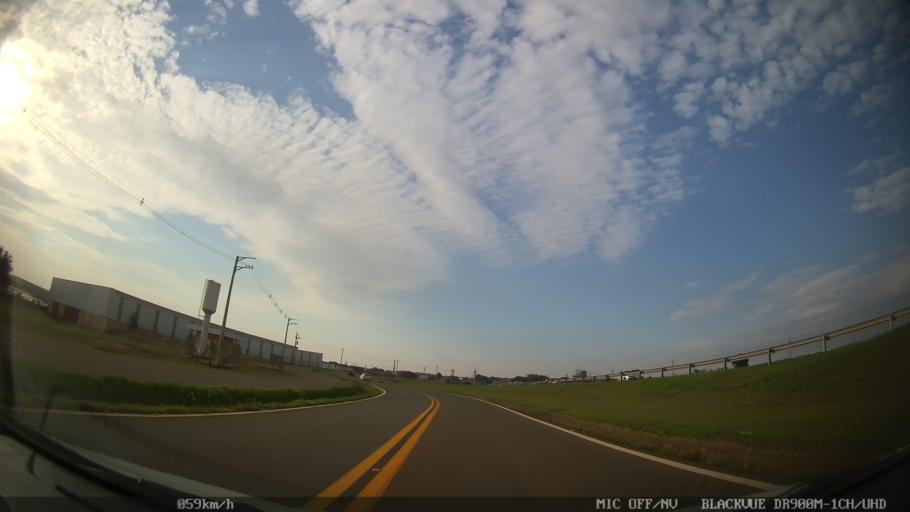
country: BR
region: Sao Paulo
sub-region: Artur Nogueira
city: Artur Nogueira
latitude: -22.5931
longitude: -47.1861
